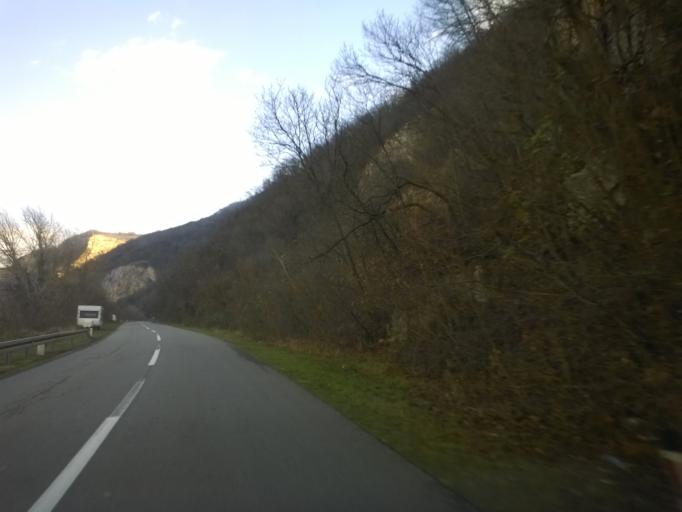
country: RO
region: Caras-Severin
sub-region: Comuna Pescari
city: Coronini
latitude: 44.6525
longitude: 21.7162
